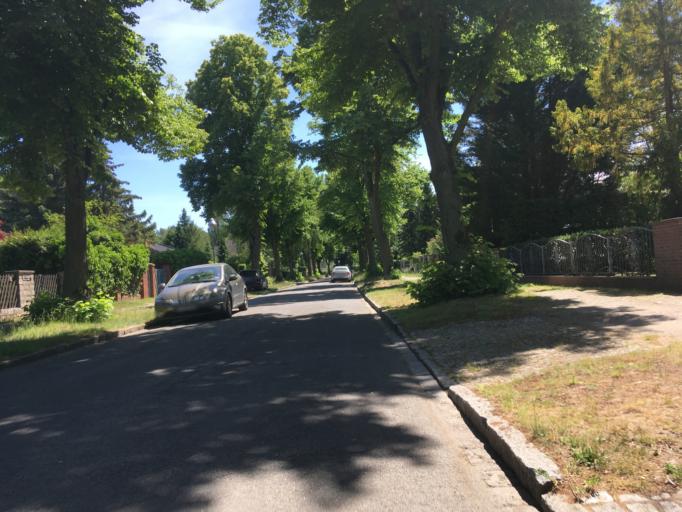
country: DE
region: Berlin
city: Schmockwitz
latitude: 52.3924
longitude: 13.6394
